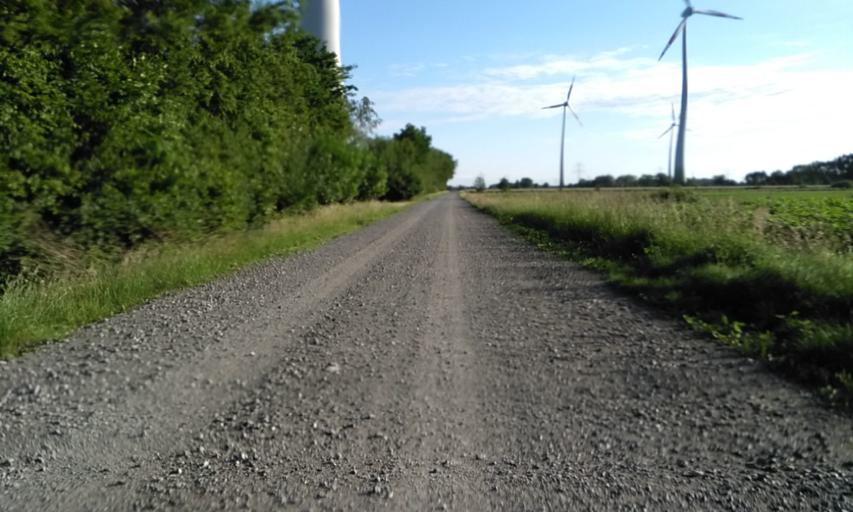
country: DE
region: Lower Saxony
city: Deinste
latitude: 53.5144
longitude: 9.4595
